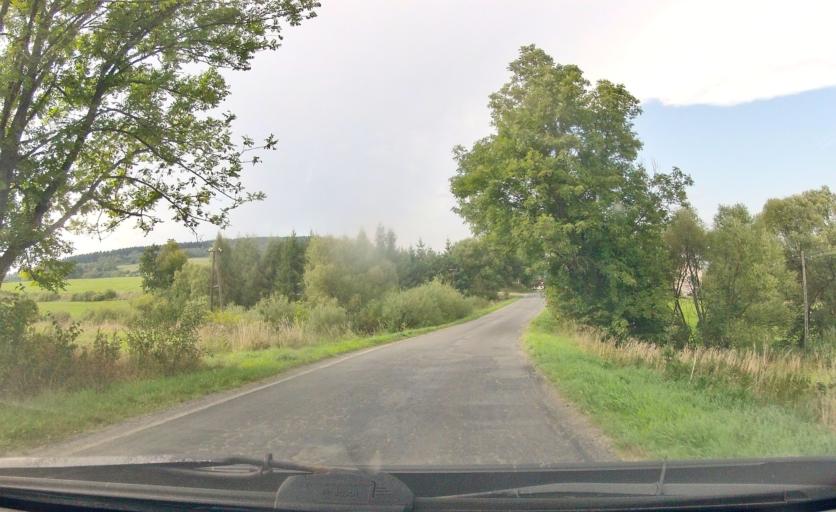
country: PL
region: Subcarpathian Voivodeship
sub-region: Powiat krosnienski
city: Dukla
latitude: 49.5189
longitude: 21.6187
